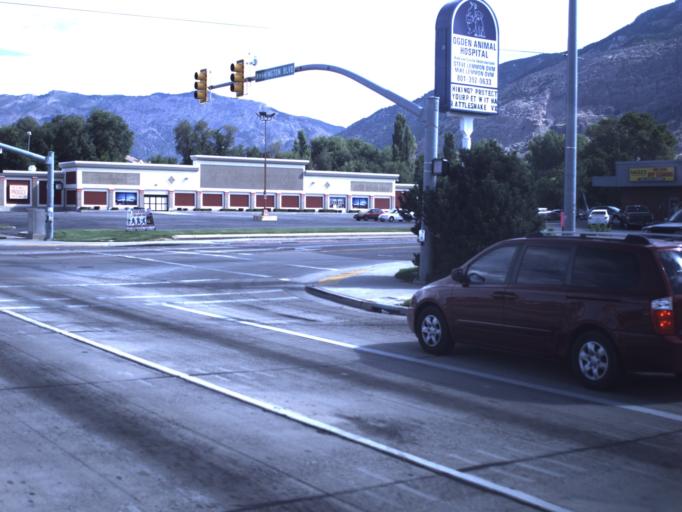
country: US
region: Utah
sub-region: Weber County
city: Harrisville
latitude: 41.2589
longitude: -111.9696
